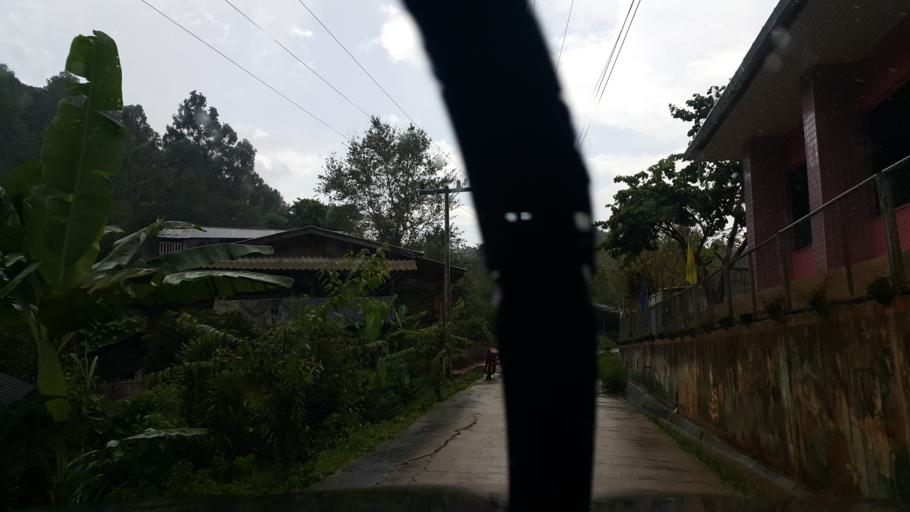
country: TH
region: Chiang Mai
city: Phrao
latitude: 19.1280
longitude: 99.3371
